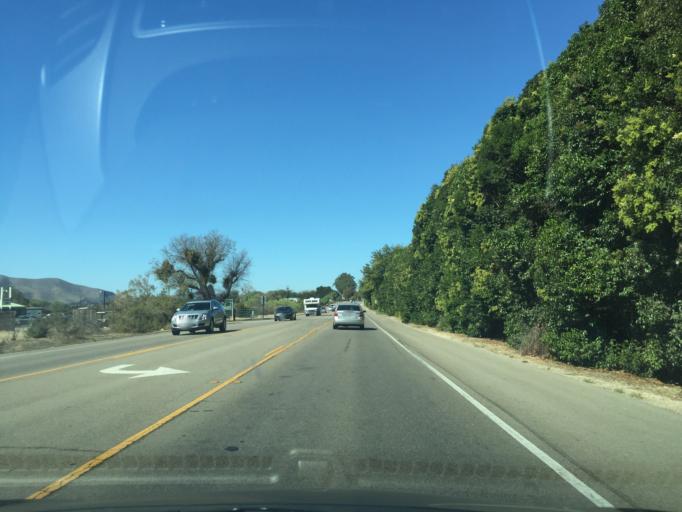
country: US
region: California
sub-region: Santa Barbara County
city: Buellton
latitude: 34.6062
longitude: -120.1754
